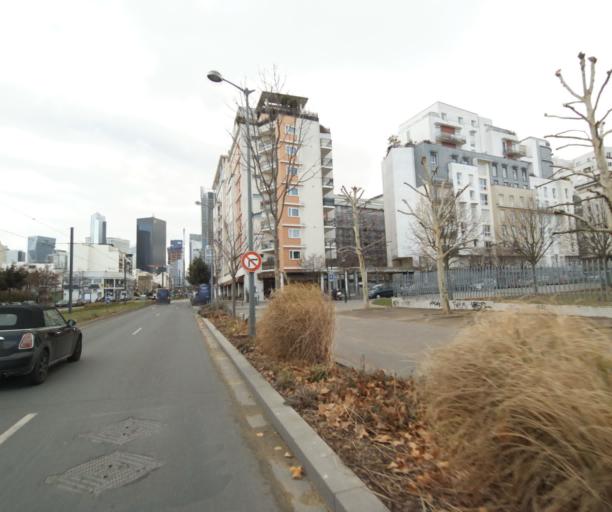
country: FR
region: Ile-de-France
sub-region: Departement des Hauts-de-Seine
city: La Garenne-Colombes
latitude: 48.9010
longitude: 2.2397
